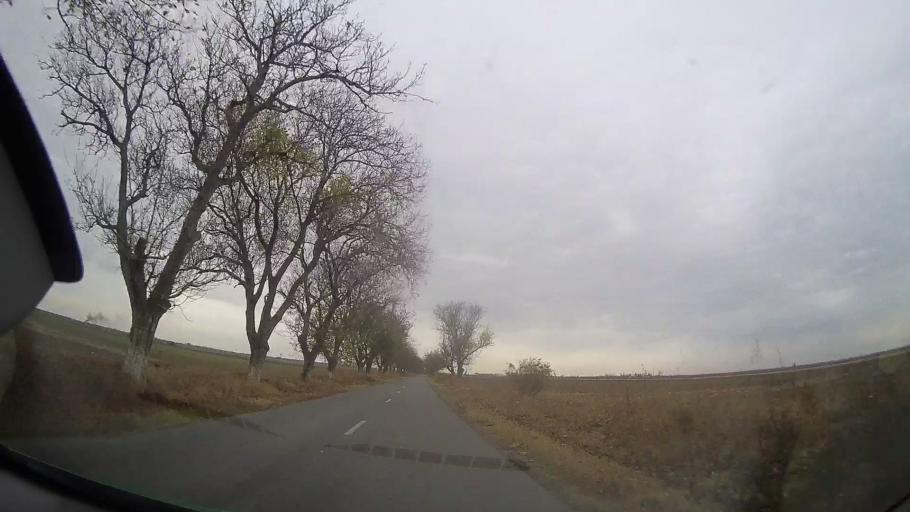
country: RO
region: Prahova
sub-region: Comuna Fantanele
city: Fantanele
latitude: 45.0135
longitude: 26.4088
